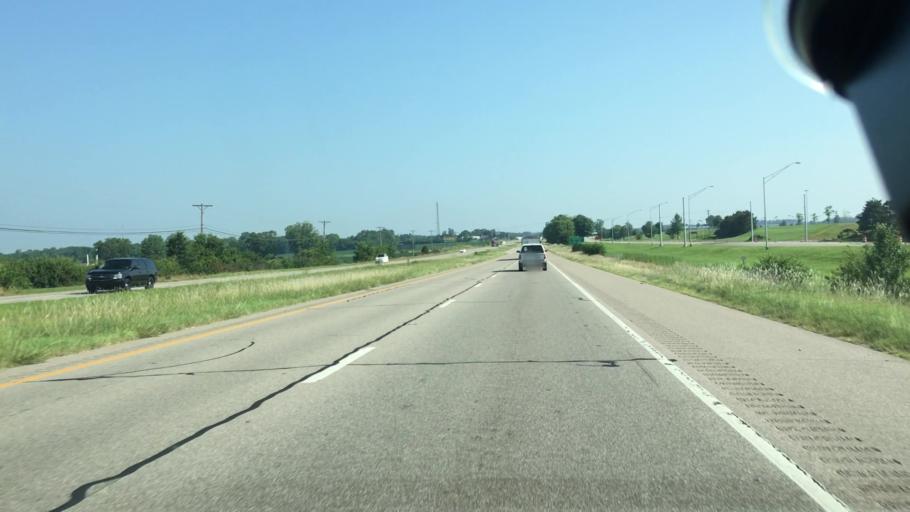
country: US
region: Indiana
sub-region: Gibson County
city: Fort Branch
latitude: 38.2933
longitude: -87.5674
